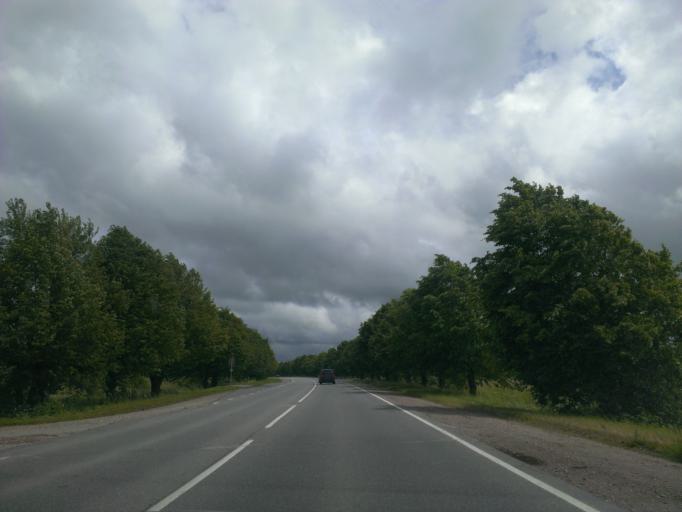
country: LV
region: Grobina
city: Grobina
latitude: 56.5331
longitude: 21.1097
